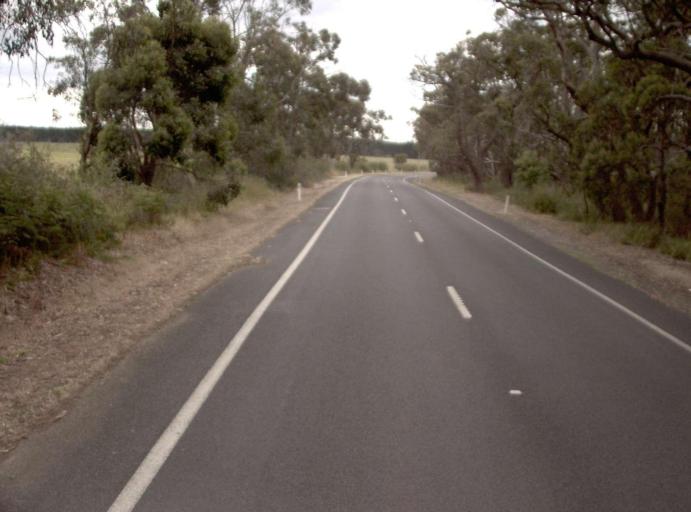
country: AU
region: Victoria
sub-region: Wellington
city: Sale
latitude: -38.2284
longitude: 147.0551
